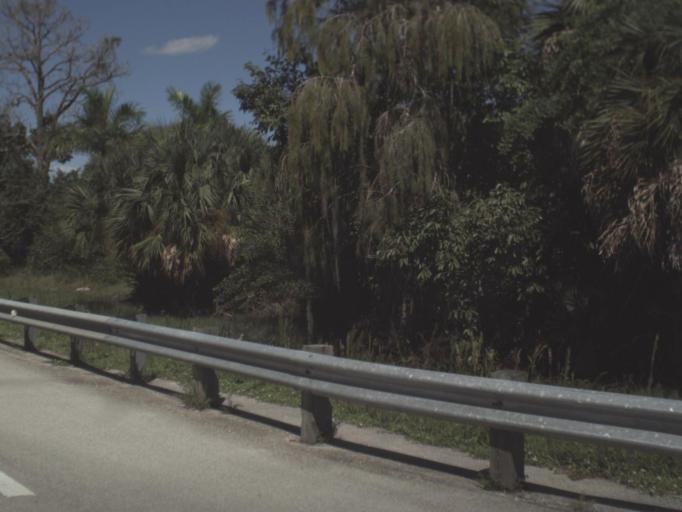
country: US
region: Florida
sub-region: Collier County
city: Lely Resort
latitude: 26.0237
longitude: -81.6372
